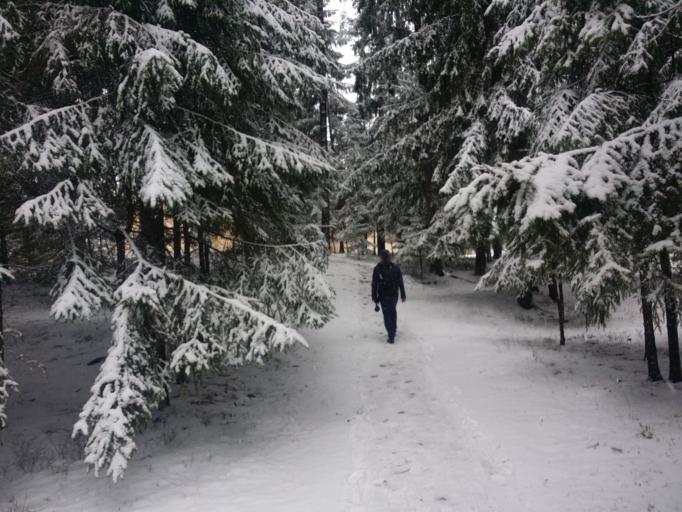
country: BY
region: Minsk
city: Rakaw
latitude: 53.9714
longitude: 27.0152
